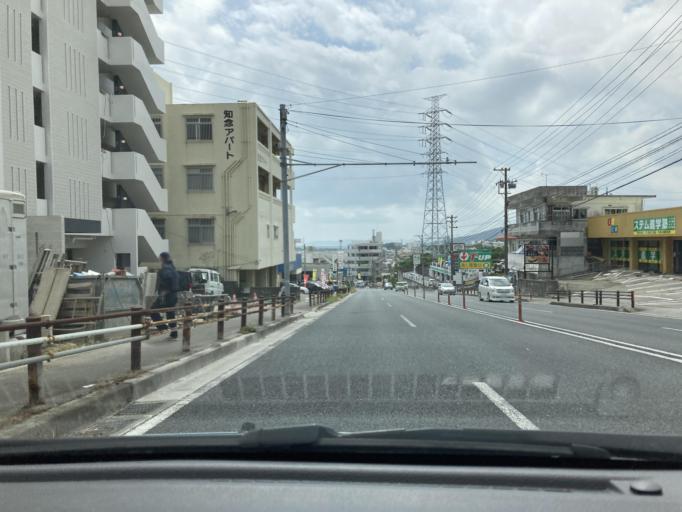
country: JP
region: Okinawa
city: Okinawa
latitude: 26.3301
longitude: 127.8224
